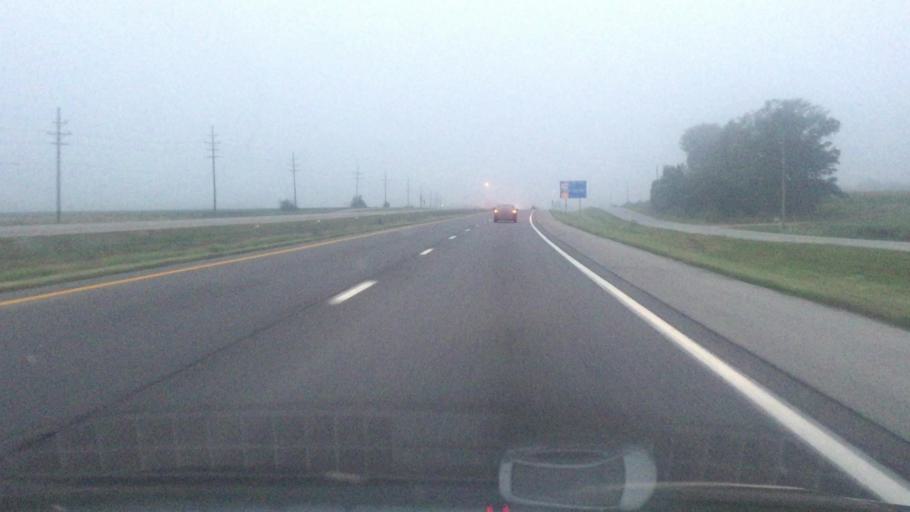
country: US
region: Missouri
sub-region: Warren County
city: Warrenton
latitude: 38.8324
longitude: -91.2169
